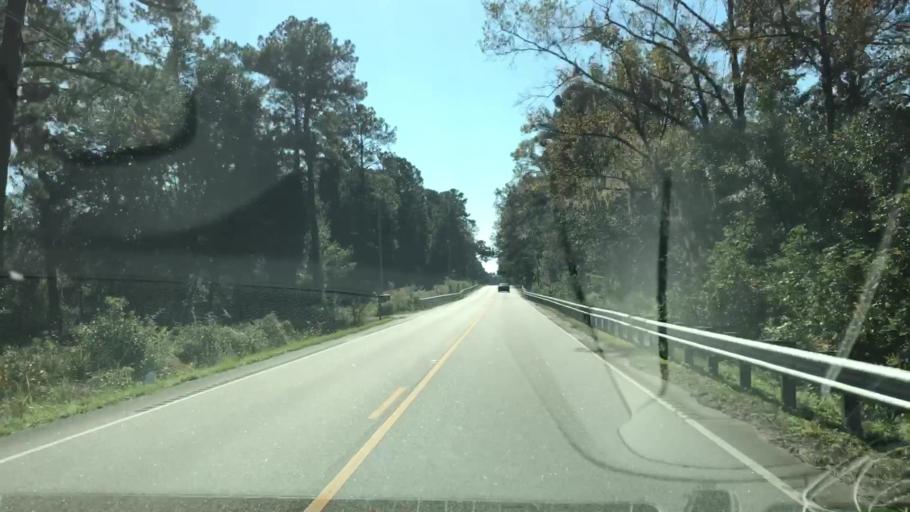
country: US
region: South Carolina
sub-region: Jasper County
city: Ridgeland
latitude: 32.5090
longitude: -80.8881
